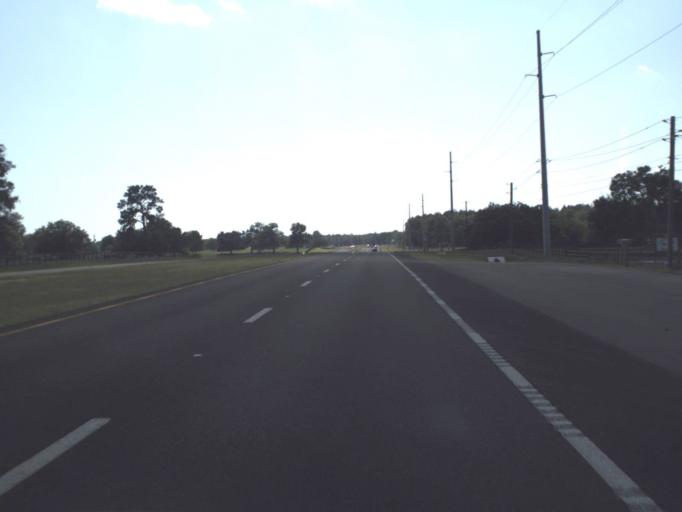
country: US
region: Florida
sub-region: Marion County
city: Ocala
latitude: 29.1869
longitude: -82.2907
